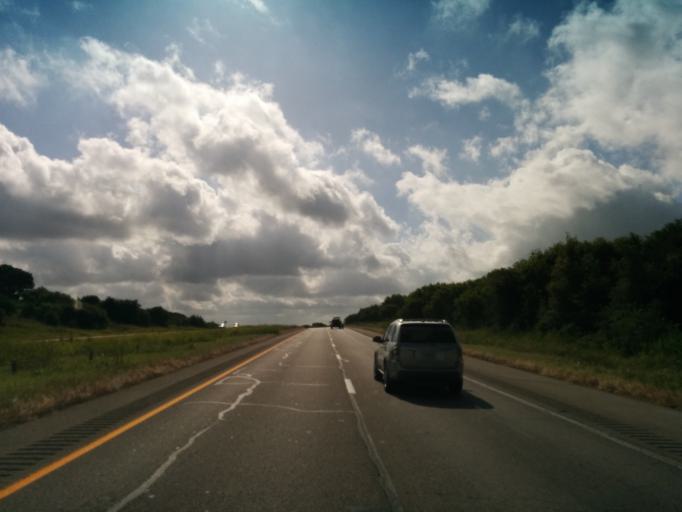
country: US
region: Texas
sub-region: Caldwell County
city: Luling
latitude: 29.6483
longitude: -97.6223
